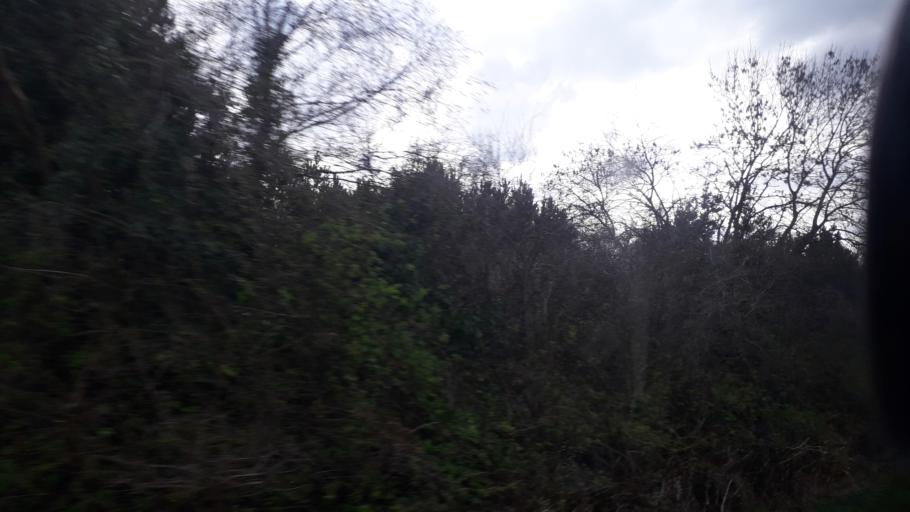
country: IE
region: Leinster
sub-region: An Iarmhi
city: Rathwire
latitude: 53.4954
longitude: -7.2338
